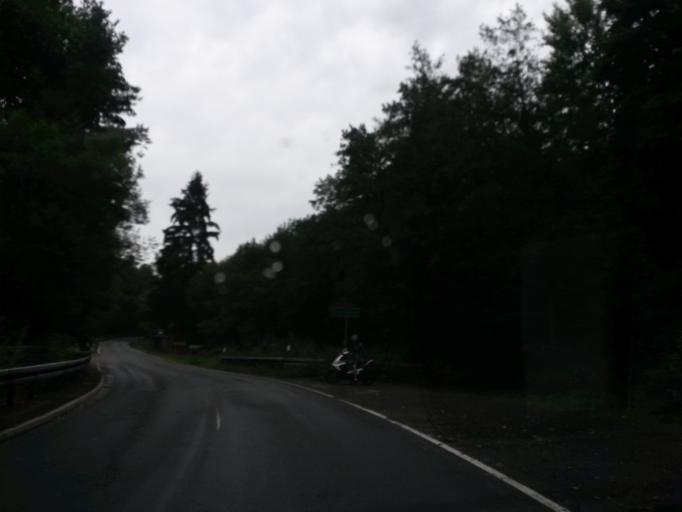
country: DE
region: North Rhine-Westphalia
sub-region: Regierungsbezirk Koln
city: Ruppichteroth
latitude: 50.8646
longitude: 7.5126
